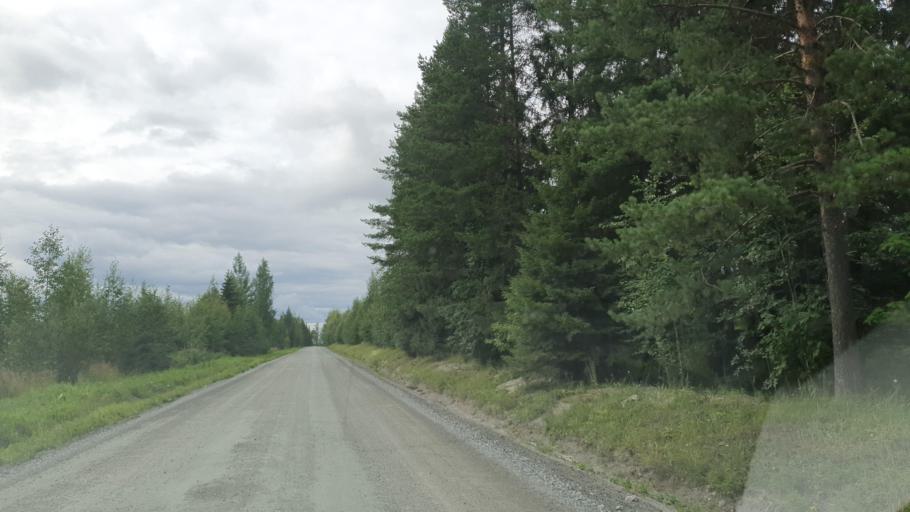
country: FI
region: Northern Savo
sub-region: Ylae-Savo
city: Iisalmi
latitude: 63.5160
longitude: 27.1102
